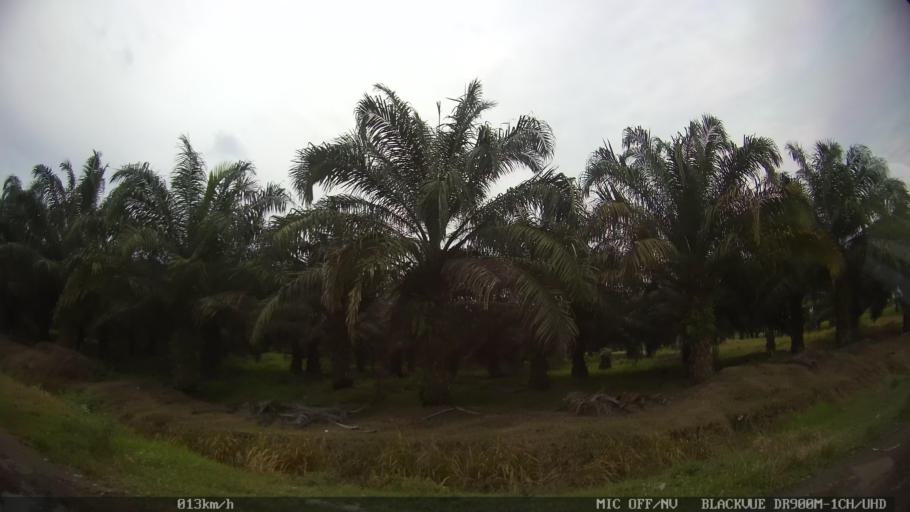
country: ID
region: North Sumatra
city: Sunggal
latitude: 3.6192
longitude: 98.5775
